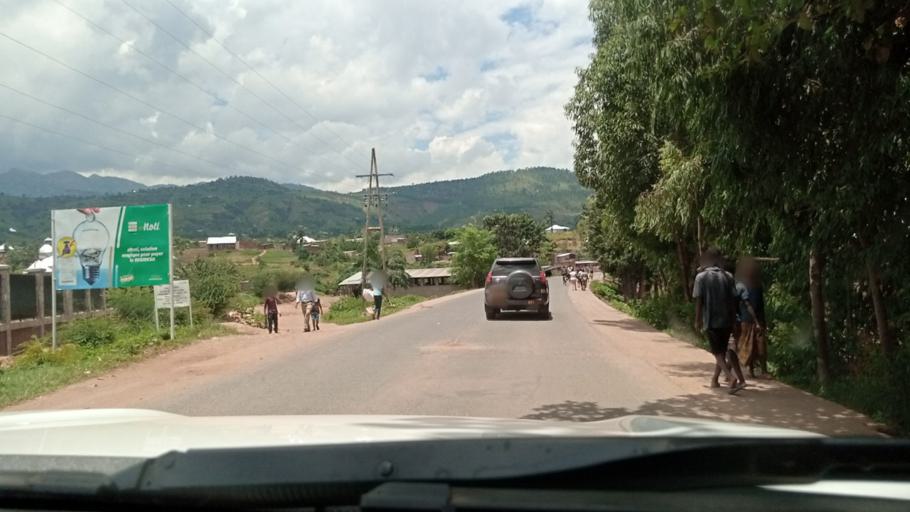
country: BI
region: Bujumbura Mairie
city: Bujumbura
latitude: -3.4788
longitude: 29.3528
